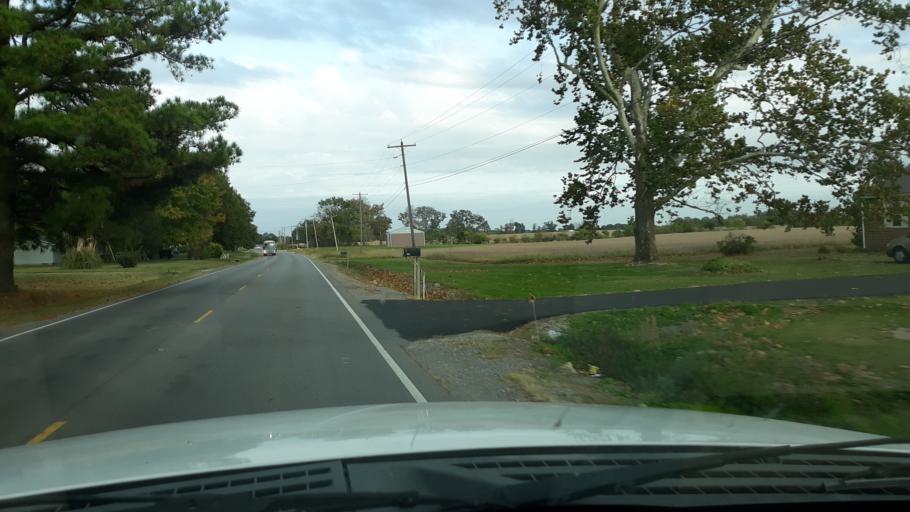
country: US
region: Illinois
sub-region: Saline County
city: Eldorado
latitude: 37.8207
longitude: -88.4836
